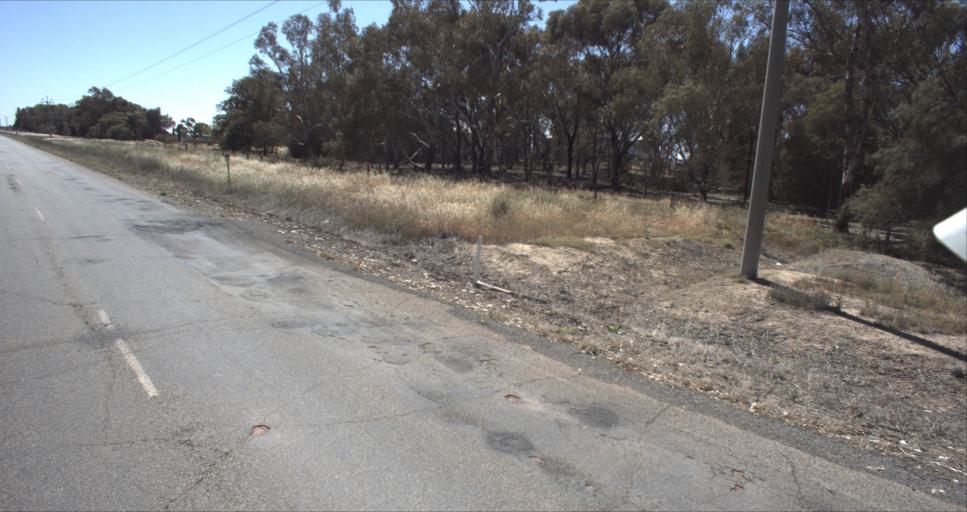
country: AU
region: New South Wales
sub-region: Leeton
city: Leeton
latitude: -34.4705
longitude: 146.2924
